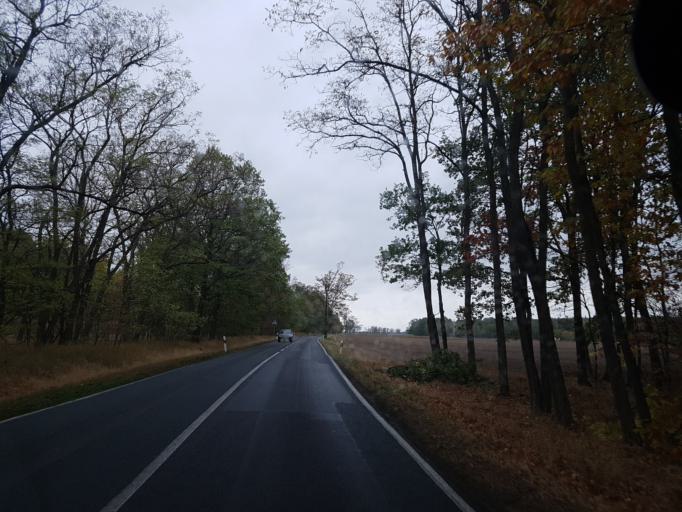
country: DE
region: Brandenburg
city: Falkenberg
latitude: 51.6153
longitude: 13.2332
